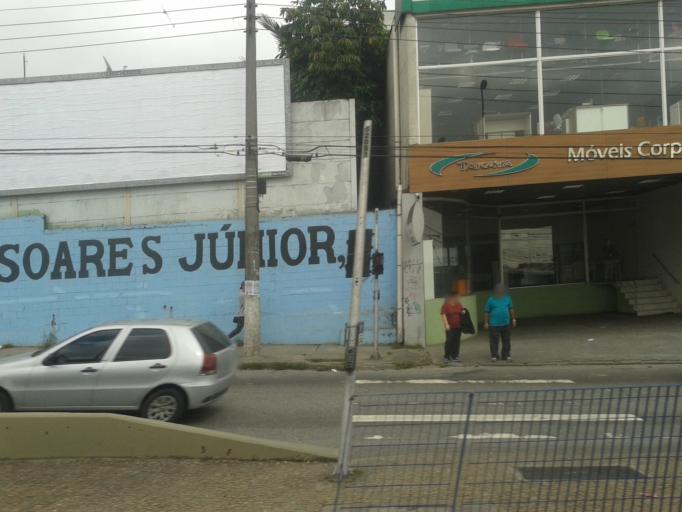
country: BR
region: Sao Paulo
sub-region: Sao Bernardo Do Campo
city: Sao Bernardo do Campo
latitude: -23.6864
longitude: -46.5928
